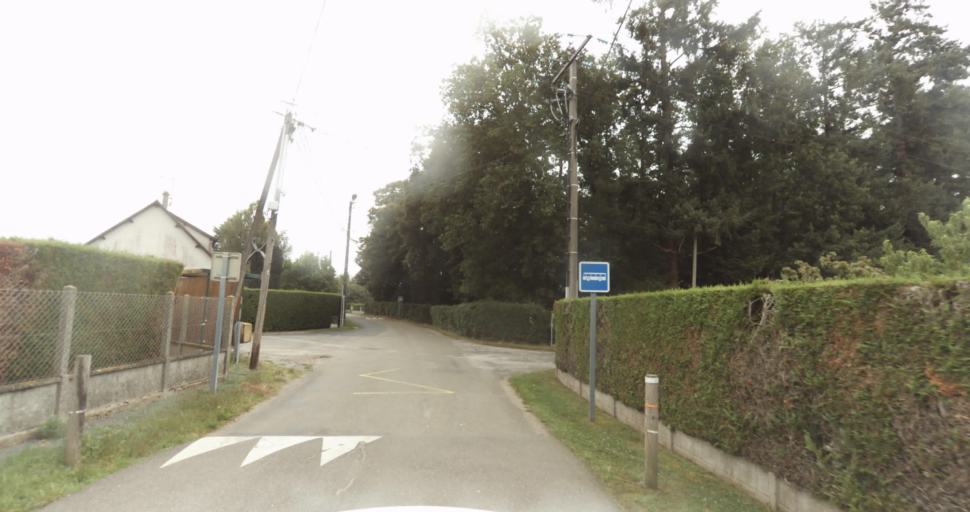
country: FR
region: Centre
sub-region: Departement d'Eure-et-Loir
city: Vert-en-Drouais
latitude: 48.7710
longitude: 1.2874
